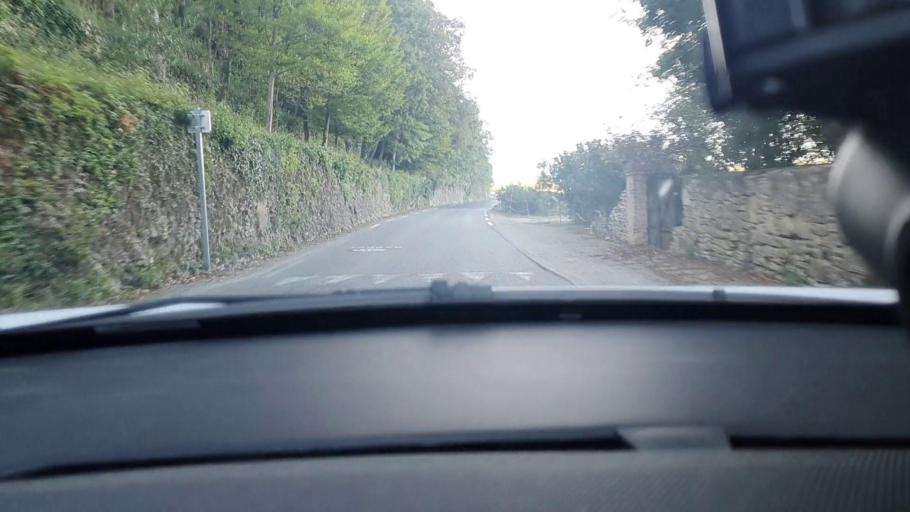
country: FR
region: Languedoc-Roussillon
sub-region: Departement du Gard
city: Barjac
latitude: 44.2366
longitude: 4.2921
